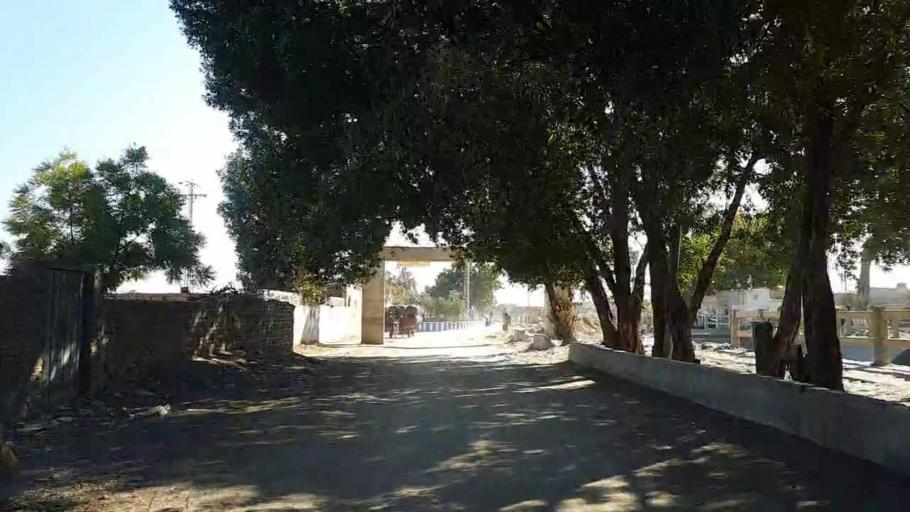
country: PK
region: Sindh
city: Nawabshah
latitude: 26.2447
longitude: 68.4221
